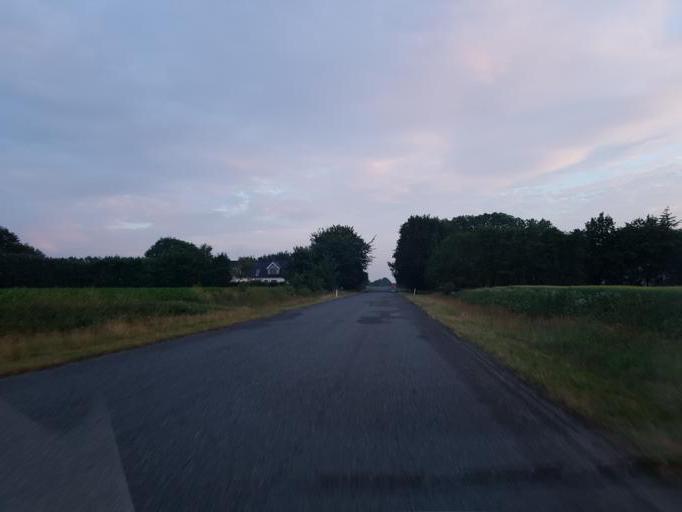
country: DK
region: South Denmark
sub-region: Esbjerg Kommune
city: Tjaereborg
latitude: 55.5187
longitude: 8.5707
